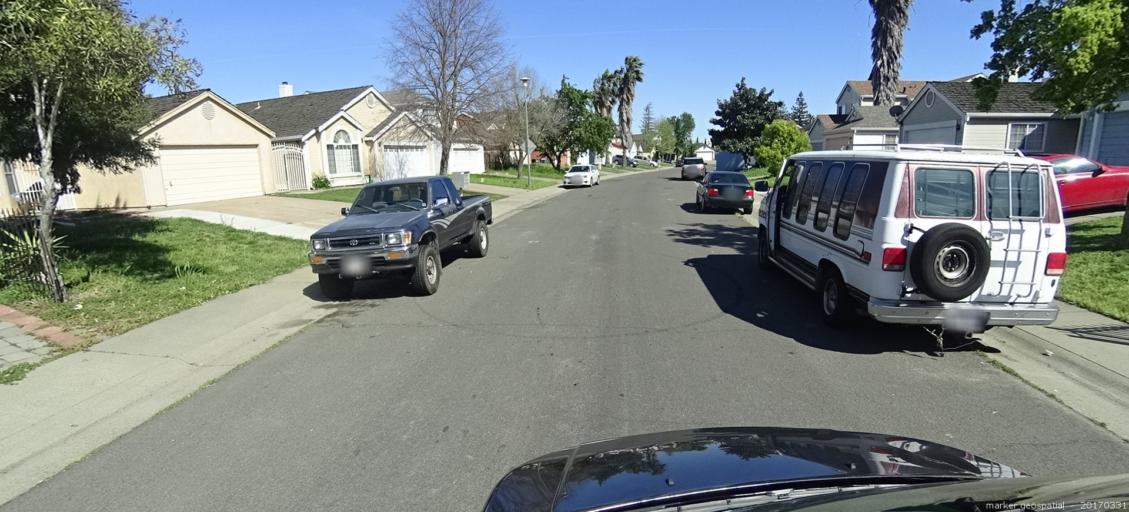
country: US
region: California
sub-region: Sacramento County
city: Parkway
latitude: 38.4616
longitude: -121.4436
